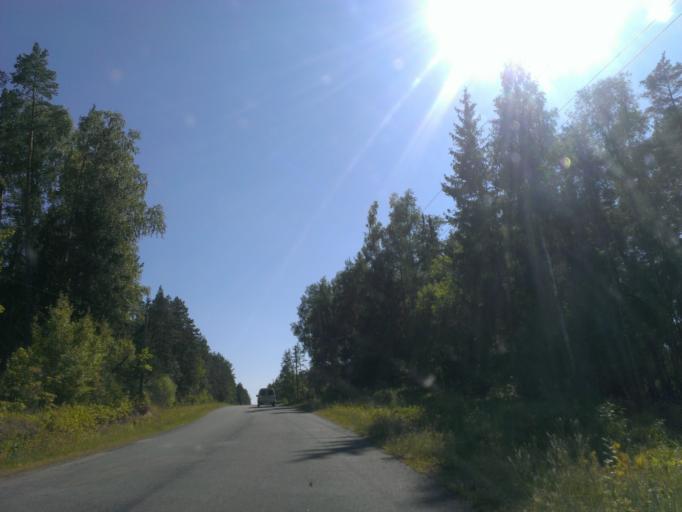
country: LV
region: Sigulda
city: Sigulda
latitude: 57.1232
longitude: 24.8272
